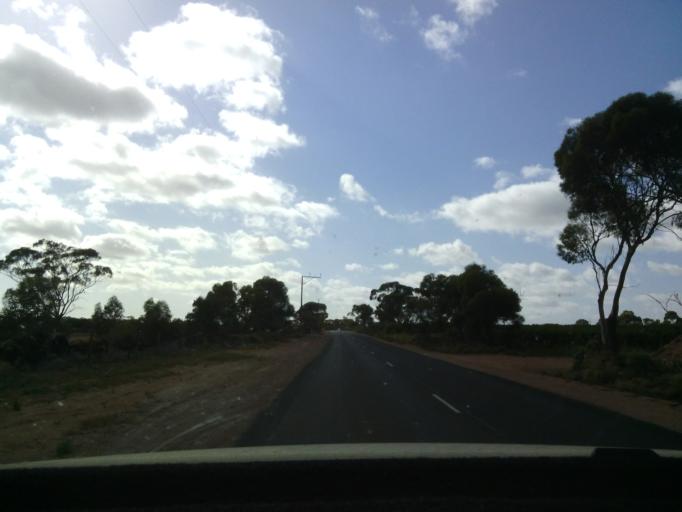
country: AU
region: South Australia
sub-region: Berri and Barmera
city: Berri
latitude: -34.2531
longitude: 140.5894
